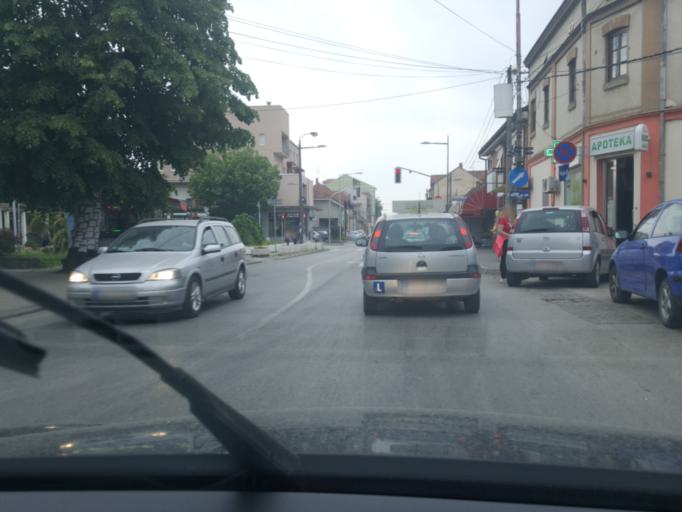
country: RS
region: Central Serbia
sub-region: Kolubarski Okrug
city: Valjevo
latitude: 44.2700
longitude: 19.8803
